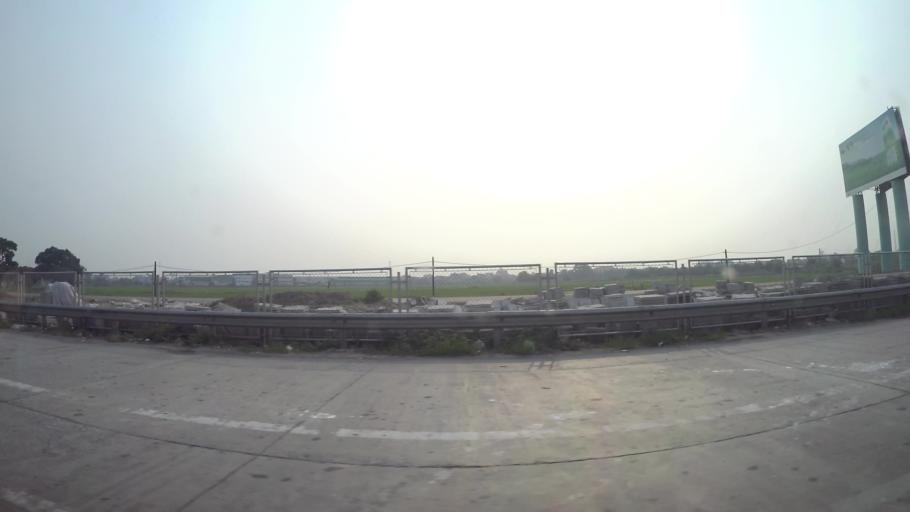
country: VN
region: Ha Noi
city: Thuong Tin
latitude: 20.9060
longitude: 105.8616
